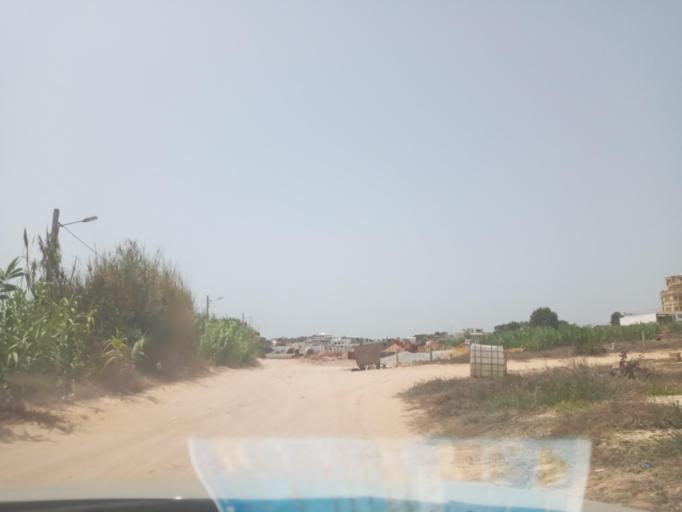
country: TN
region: Nabul
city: El Haouaria
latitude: 37.0311
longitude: 11.0569
